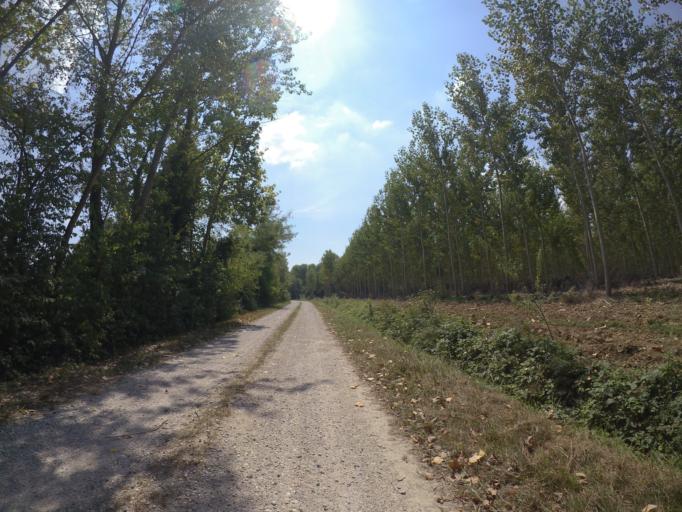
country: IT
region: Friuli Venezia Giulia
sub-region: Provincia di Udine
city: Bertiolo
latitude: 45.9125
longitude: 13.0611
